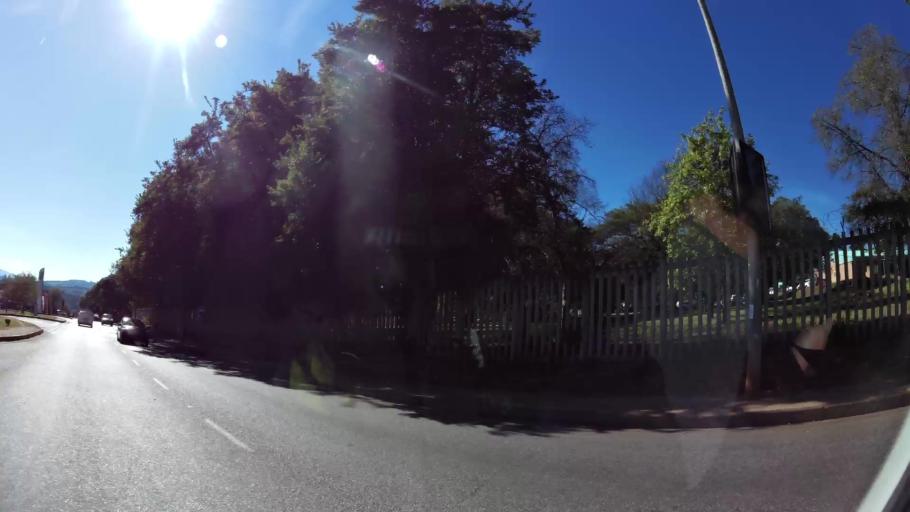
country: ZA
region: Limpopo
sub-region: Mopani District Municipality
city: Tzaneen
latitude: -23.8344
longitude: 30.1632
